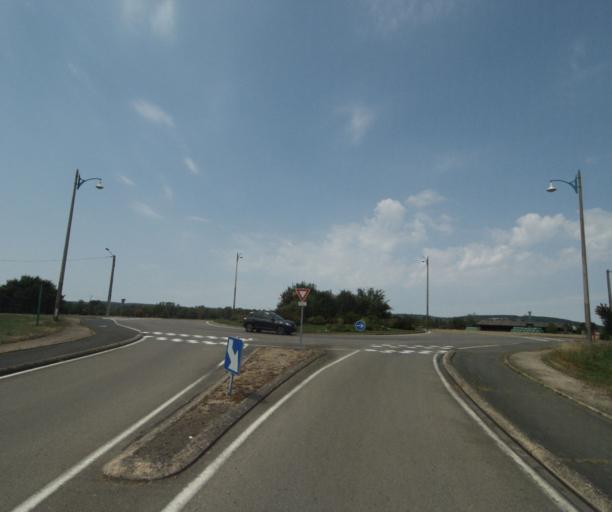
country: FR
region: Bourgogne
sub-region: Departement de Saone-et-Loire
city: Gueugnon
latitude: 46.5903
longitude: 4.0658
